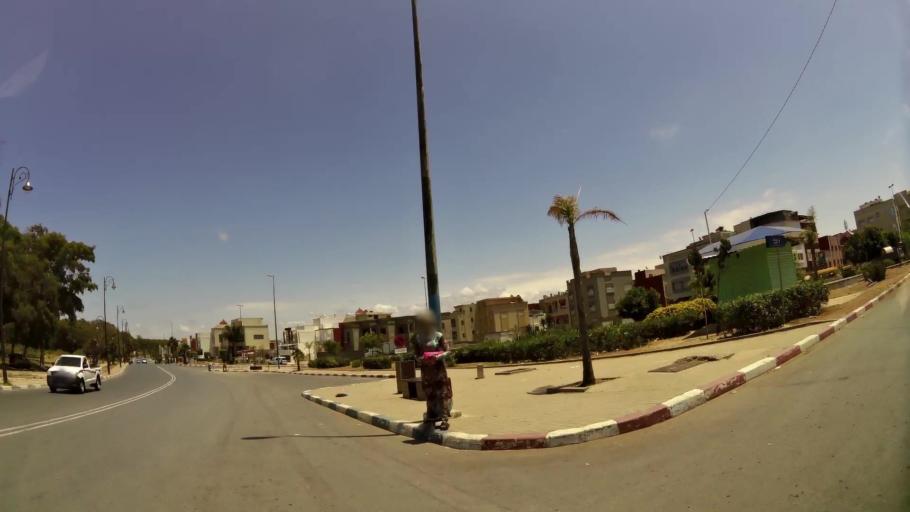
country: MA
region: Gharb-Chrarda-Beni Hssen
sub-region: Kenitra Province
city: Kenitra
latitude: 34.2667
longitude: -6.6446
